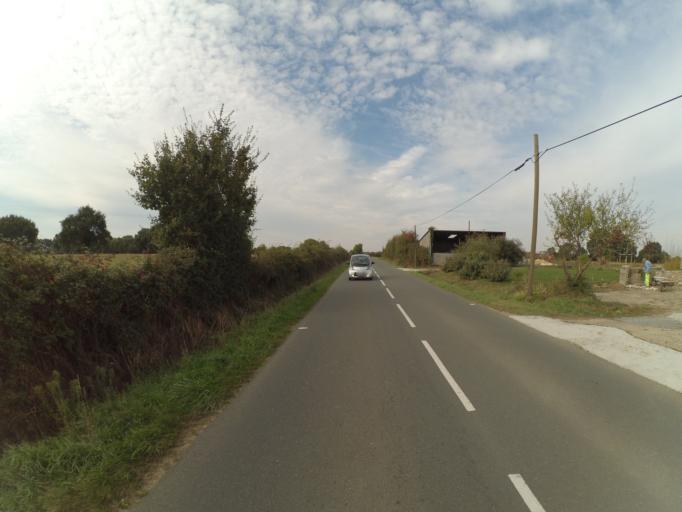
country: FR
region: Pays de la Loire
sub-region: Departement de Maine-et-Loire
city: Melay
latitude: 47.2076
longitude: -0.6677
